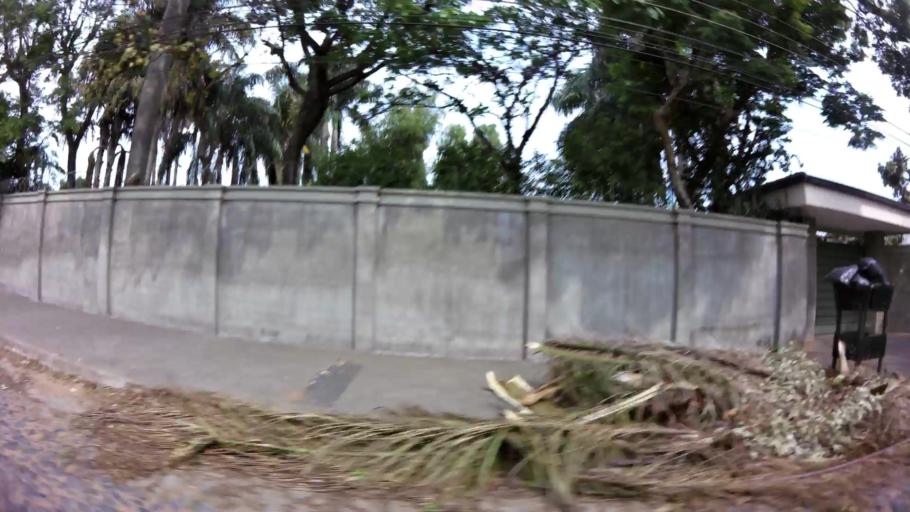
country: PY
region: Central
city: Fernando de la Mora
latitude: -25.2765
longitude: -57.5567
